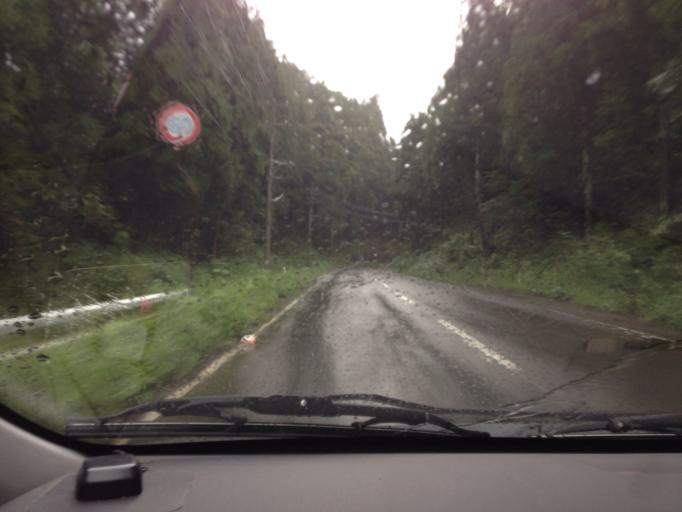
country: JP
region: Fukushima
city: Koriyama
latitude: 37.4385
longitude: 140.2620
